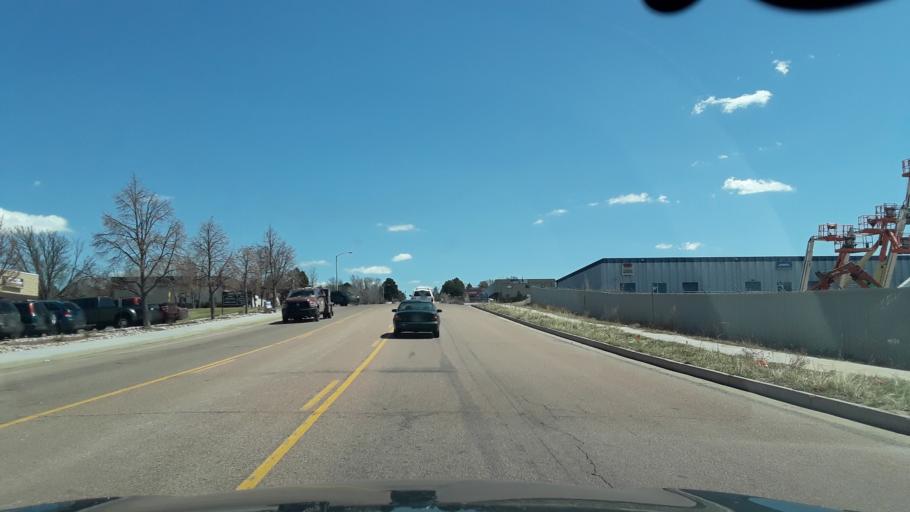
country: US
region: Colorado
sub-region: El Paso County
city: Cimarron Hills
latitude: 38.8462
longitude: -104.7130
